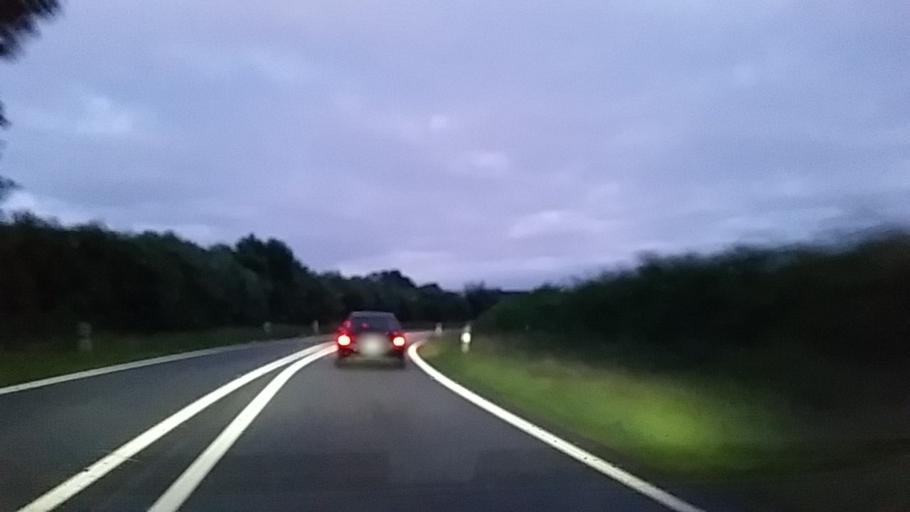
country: DE
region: Schleswig-Holstein
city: Siek
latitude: 53.6429
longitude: 10.2823
